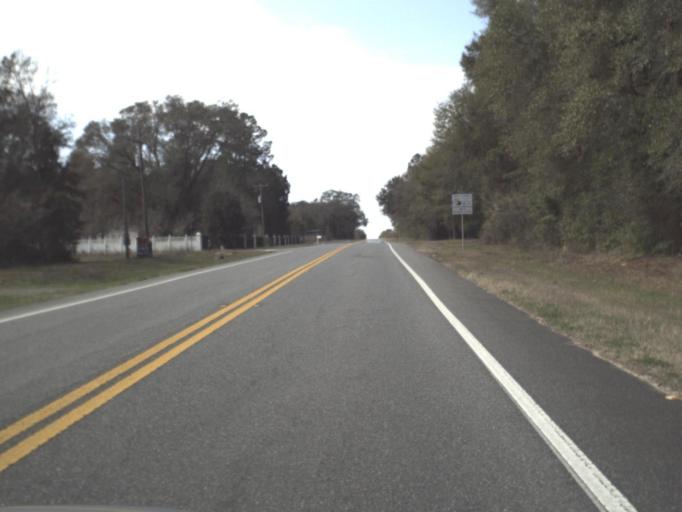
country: US
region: Florida
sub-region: Gadsden County
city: Gretna
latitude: 30.5320
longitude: -84.7750
